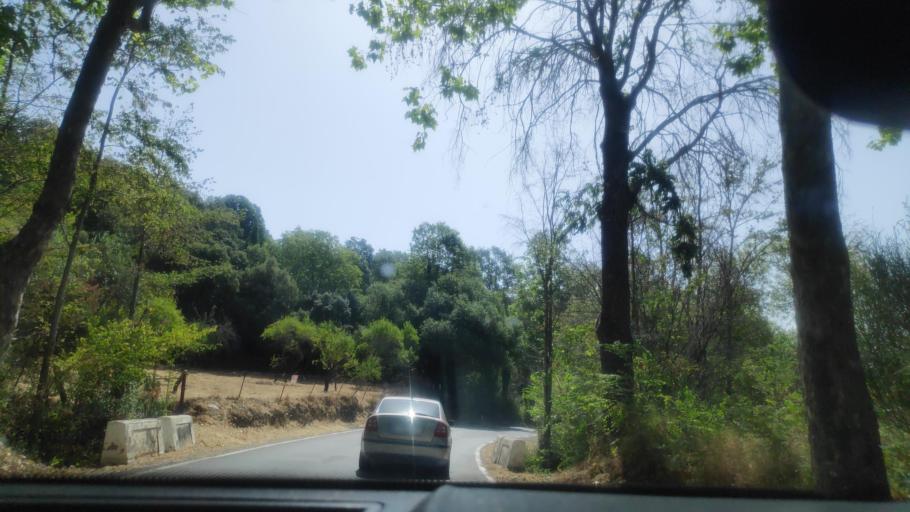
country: ES
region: Andalusia
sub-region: Provincia de Granada
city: Portugos
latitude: 36.9403
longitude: -3.3048
